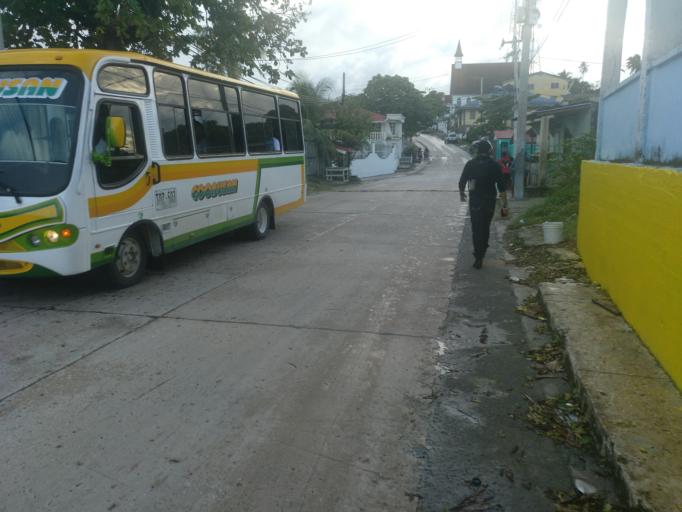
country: CO
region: Archipielago de San Andres, Providencia y Santa Catalina
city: San Andres
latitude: 12.5632
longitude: -81.7158
